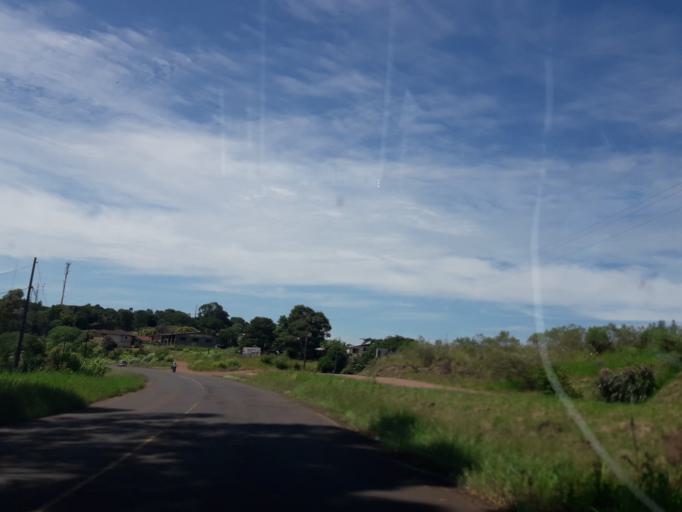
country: AR
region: Misiones
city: Bernardo de Irigoyen
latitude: -26.5852
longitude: -53.5187
